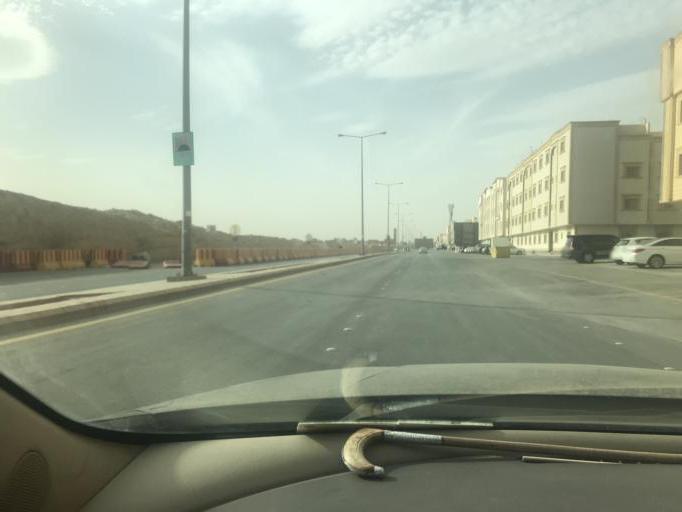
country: SA
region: Ar Riyad
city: Riyadh
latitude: 24.7941
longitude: 46.6685
